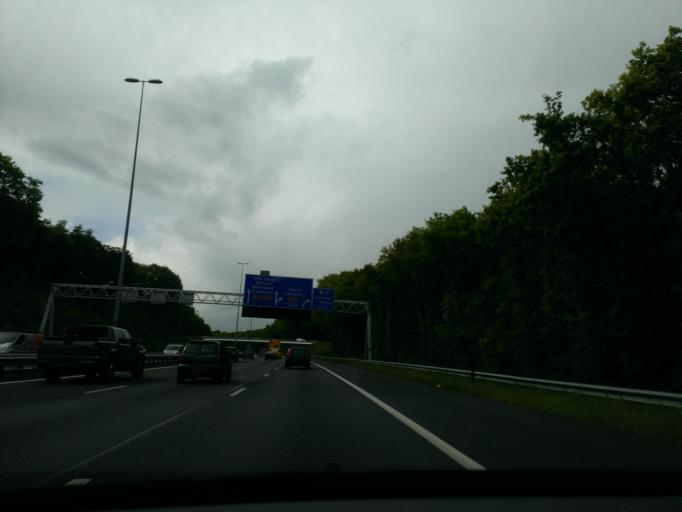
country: NL
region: Gelderland
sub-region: Gemeente Rozendaal
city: Rozendaal
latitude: 52.0085
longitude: 5.9450
